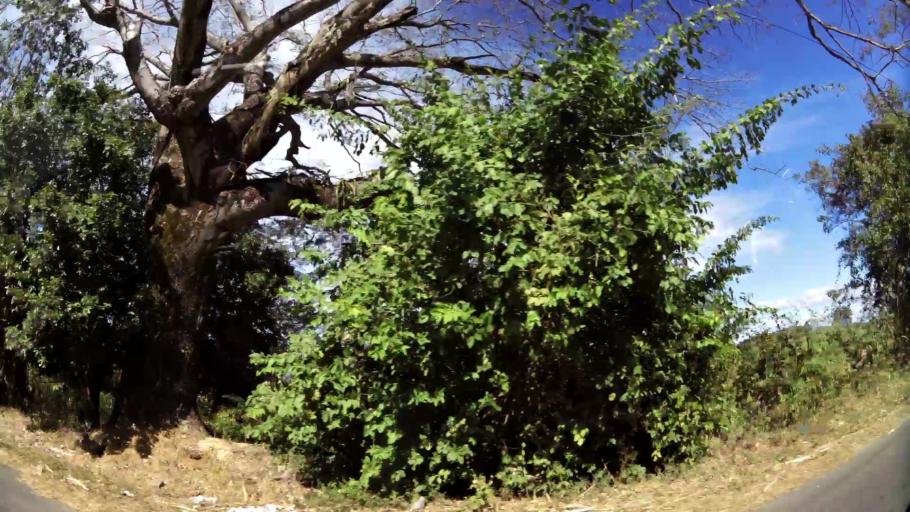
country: SV
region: San Salvador
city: Aguilares
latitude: 13.9622
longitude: -89.1106
